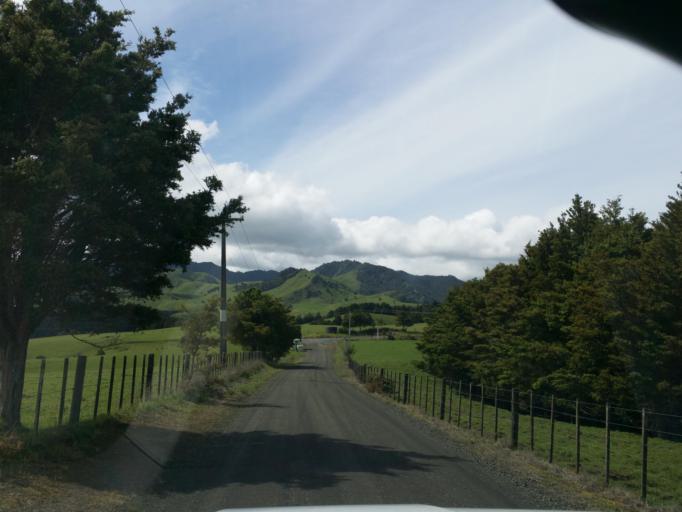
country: NZ
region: Northland
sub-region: Kaipara District
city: Dargaville
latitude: -35.8377
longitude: 174.0279
